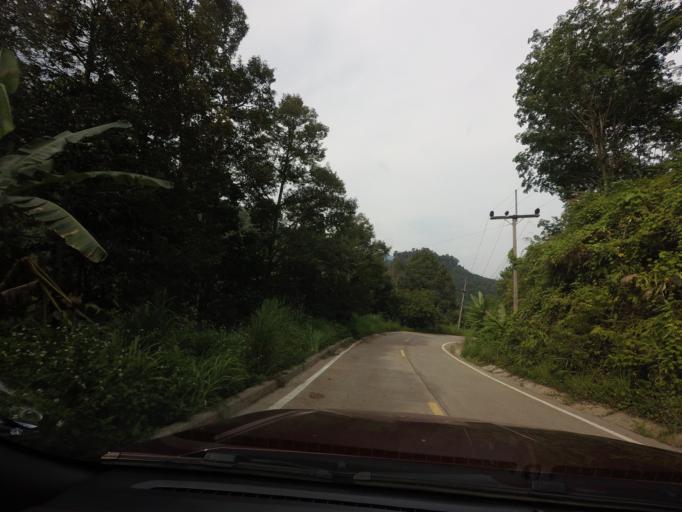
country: TH
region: Yala
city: Than To
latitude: 6.0690
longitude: 101.3540
